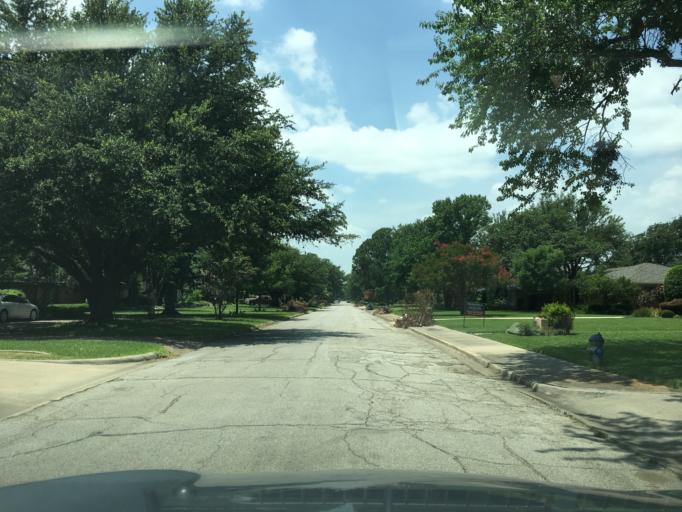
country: US
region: Texas
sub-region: Dallas County
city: Addison
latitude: 32.9175
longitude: -96.8041
